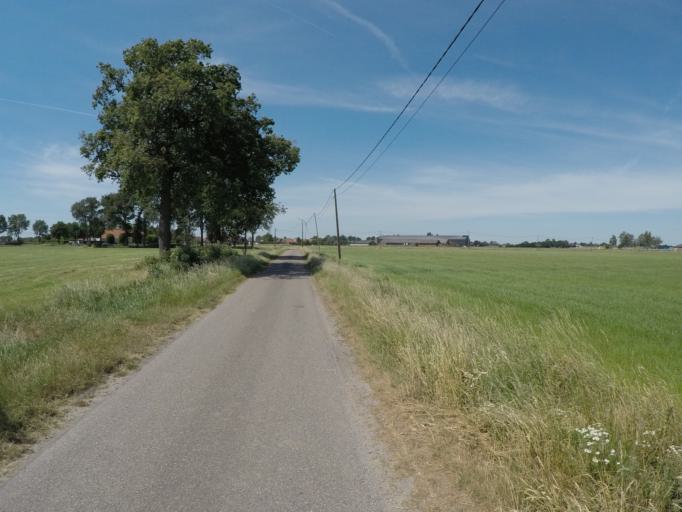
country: BE
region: Flanders
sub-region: Provincie Antwerpen
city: Brecht
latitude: 51.3863
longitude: 4.6865
